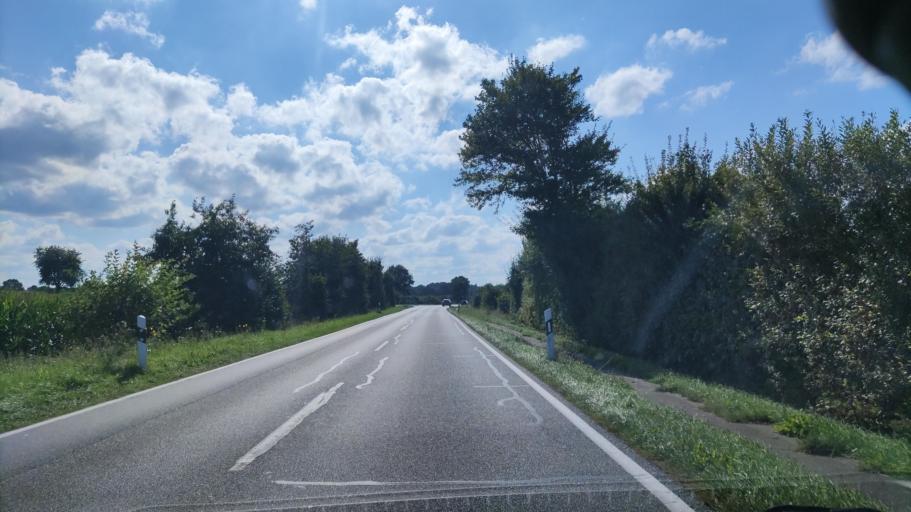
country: DE
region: Schleswig-Holstein
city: Neu Duvenstedt
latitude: 54.4017
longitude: 9.6682
